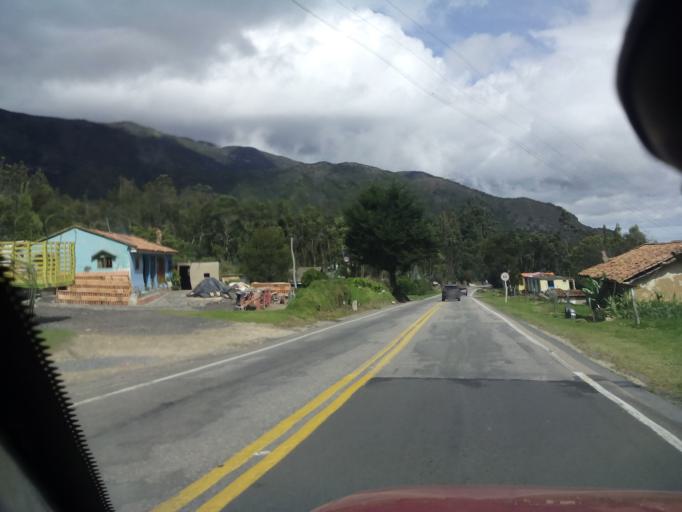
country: CO
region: Boyaca
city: Arcabuco
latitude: 5.7306
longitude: -73.3983
